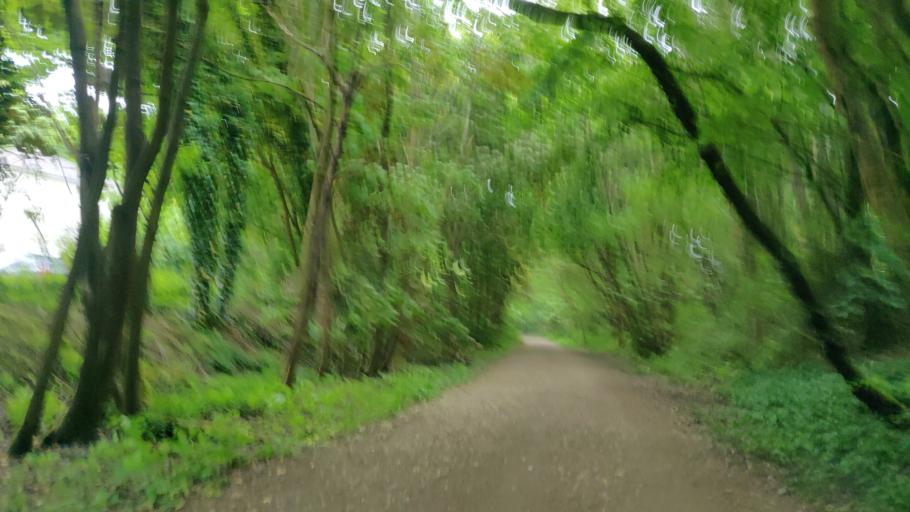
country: GB
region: England
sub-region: West Sussex
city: Southwater
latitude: 51.0419
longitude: -0.3703
